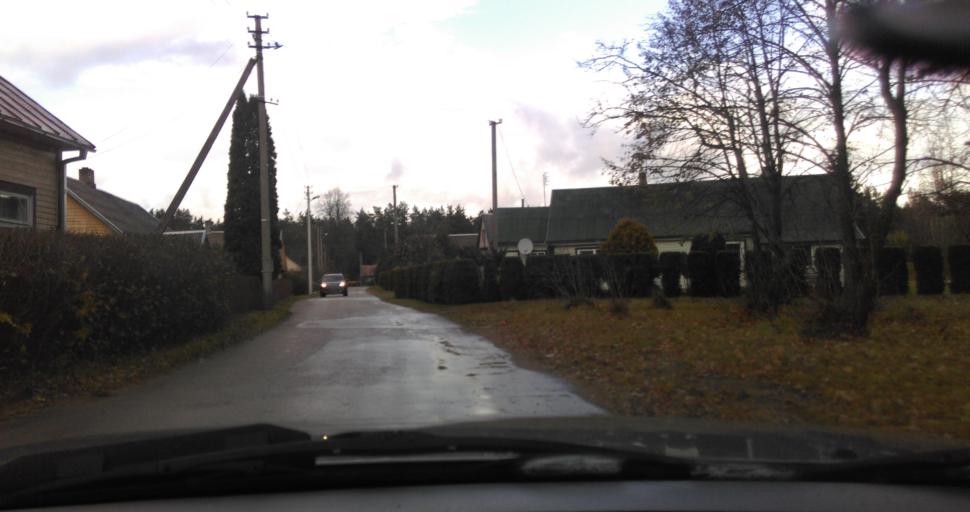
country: LT
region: Utenos apskritis
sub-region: Utena
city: Utena
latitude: 55.5881
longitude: 25.4979
